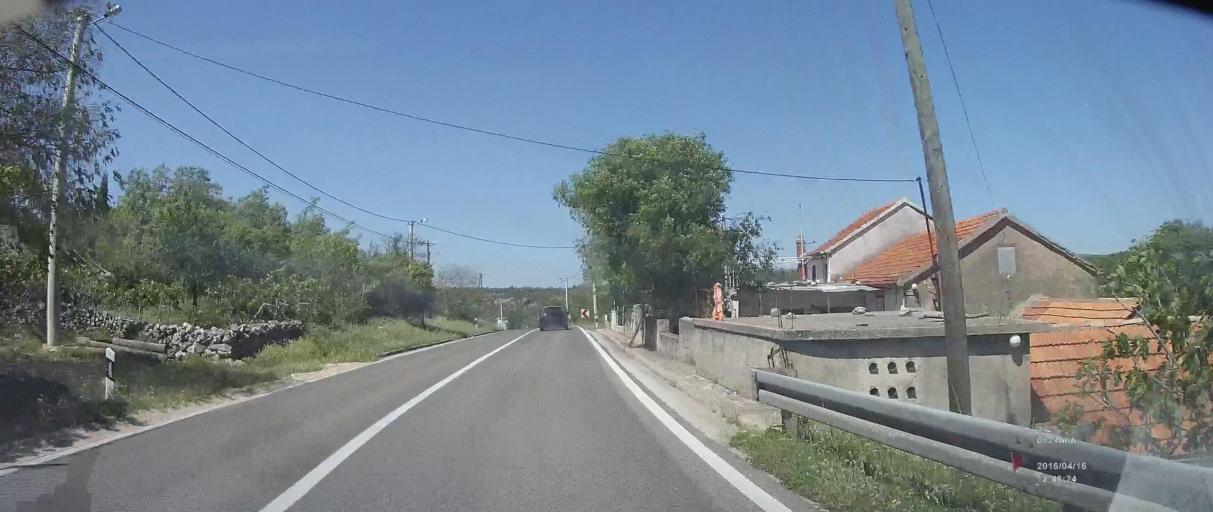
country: HR
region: Sibensko-Kniniska
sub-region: Grad Sibenik
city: Brodarica
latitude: 43.6704
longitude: 16.0385
